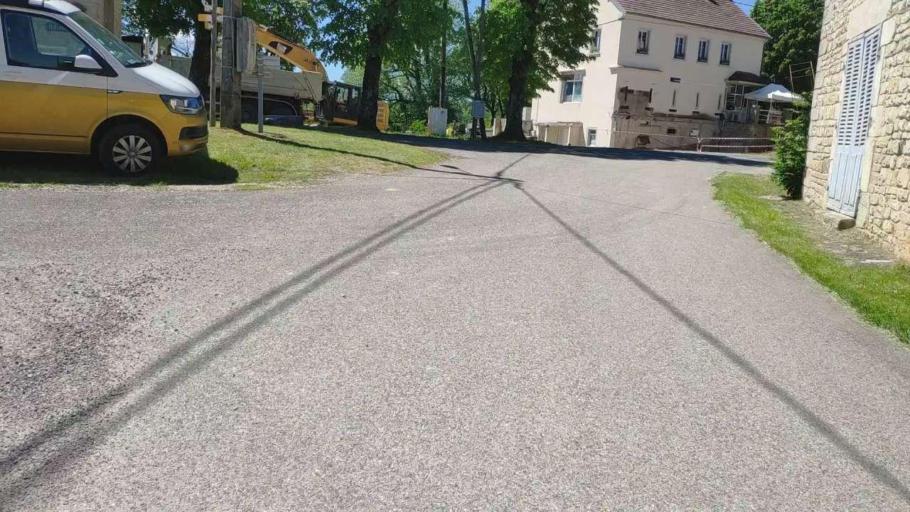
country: FR
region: Franche-Comte
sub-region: Departement du Jura
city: Perrigny
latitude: 46.7139
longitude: 5.6458
